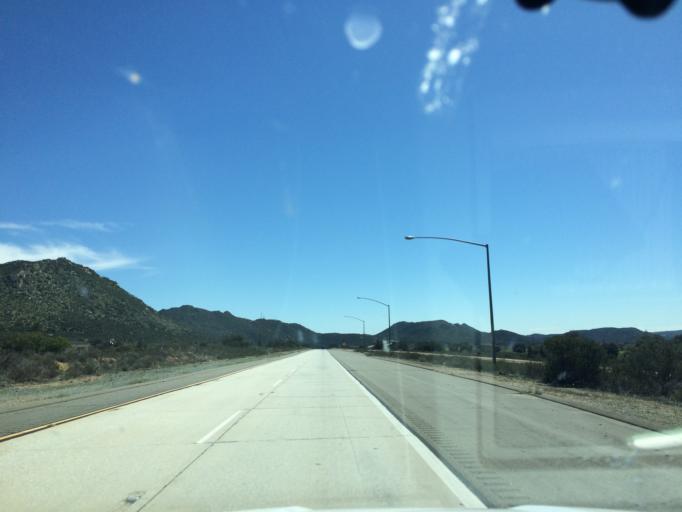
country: US
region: California
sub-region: San Diego County
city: Pine Valley
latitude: 32.7609
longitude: -116.4867
